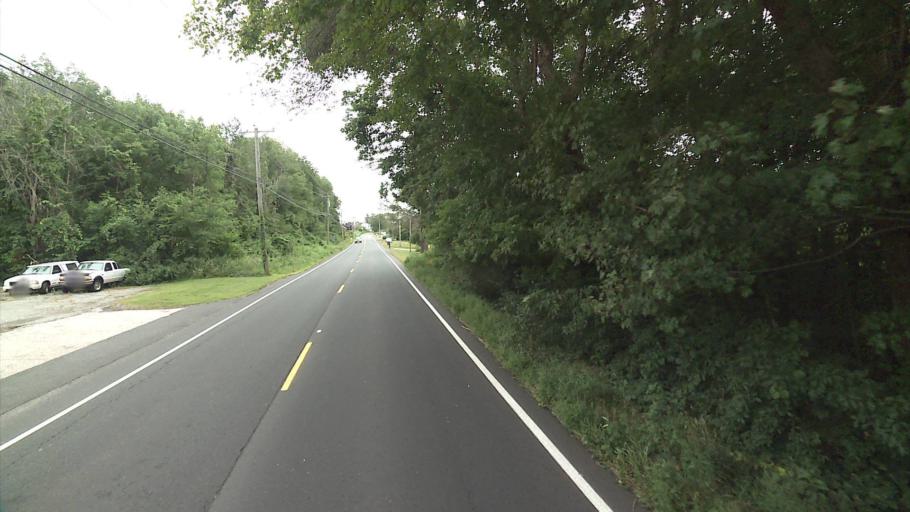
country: US
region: Connecticut
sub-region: New London County
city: Colchester
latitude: 41.5360
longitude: -72.3007
